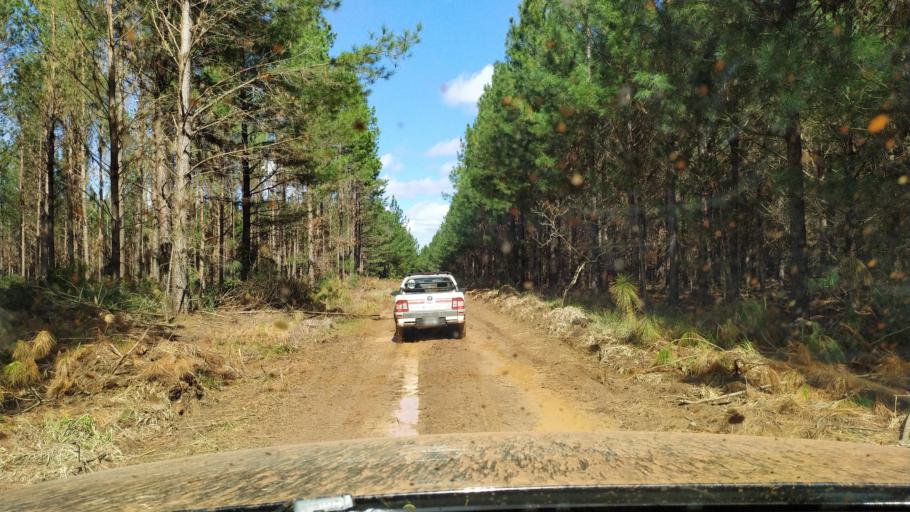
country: AR
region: Corrientes
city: Santo Tome
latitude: -28.4073
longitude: -56.0159
